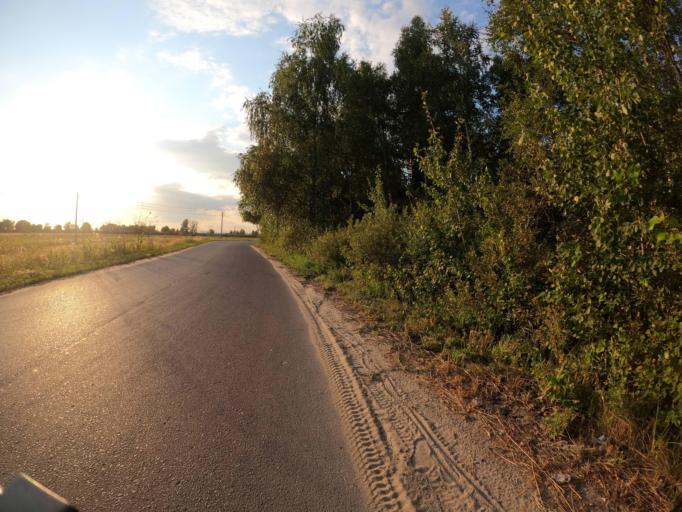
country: RU
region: Moskovskaya
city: Malyshevo
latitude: 55.5161
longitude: 38.2844
